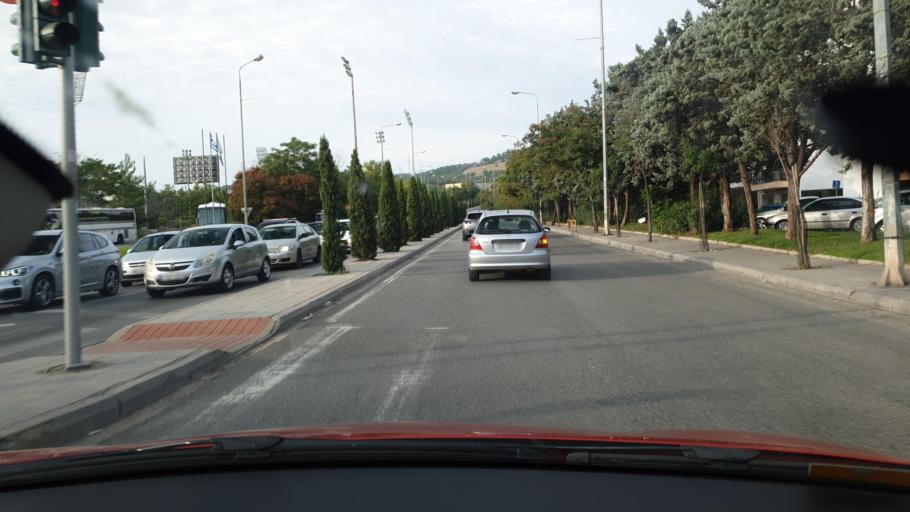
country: GR
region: Central Macedonia
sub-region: Nomos Thessalonikis
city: Triandria
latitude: 40.6221
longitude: 22.9674
